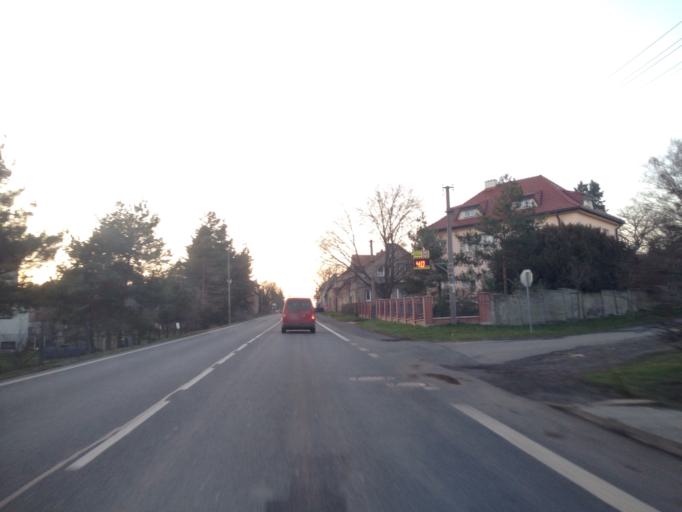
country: CZ
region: Central Bohemia
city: Revnicov
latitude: 50.1813
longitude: 13.8121
